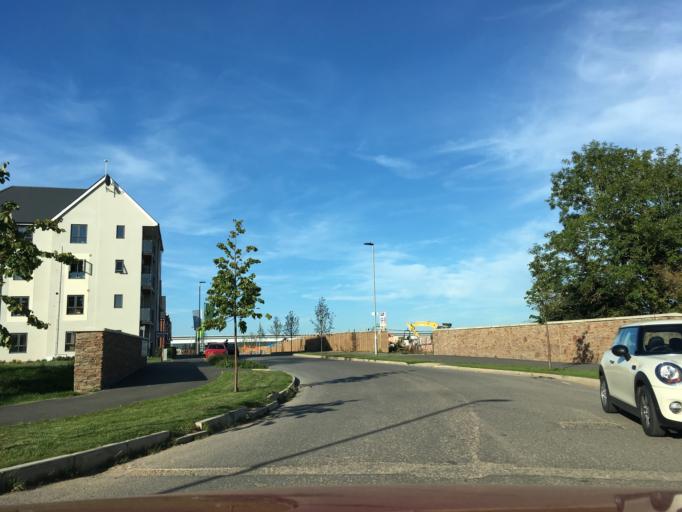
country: GB
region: England
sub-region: South Gloucestershire
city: Siston
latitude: 51.4997
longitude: -2.4690
